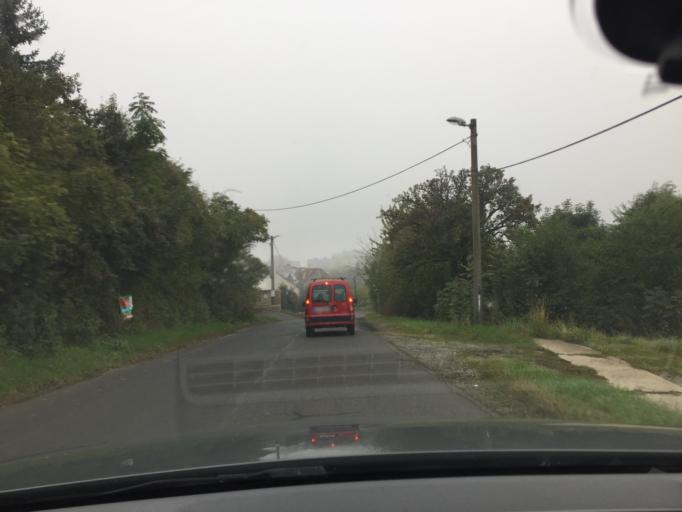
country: CZ
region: Ustecky
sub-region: Okres Usti nad Labem
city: Usti nad Labem
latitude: 50.6838
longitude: 14.0386
